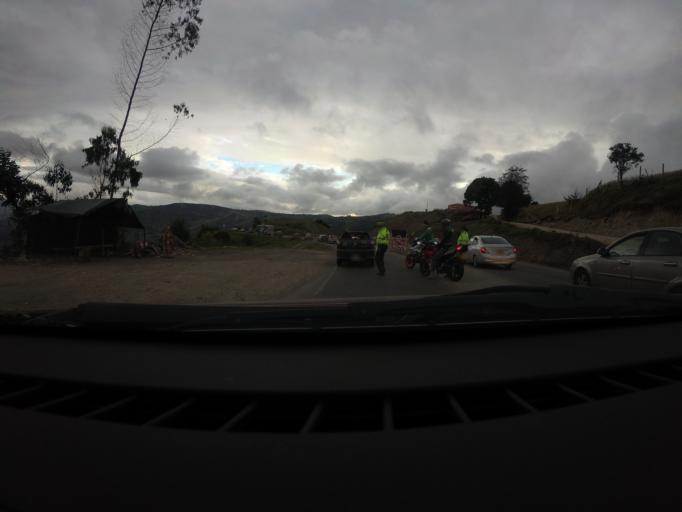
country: CO
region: Boyaca
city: Samaca
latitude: 5.4592
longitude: -73.4198
